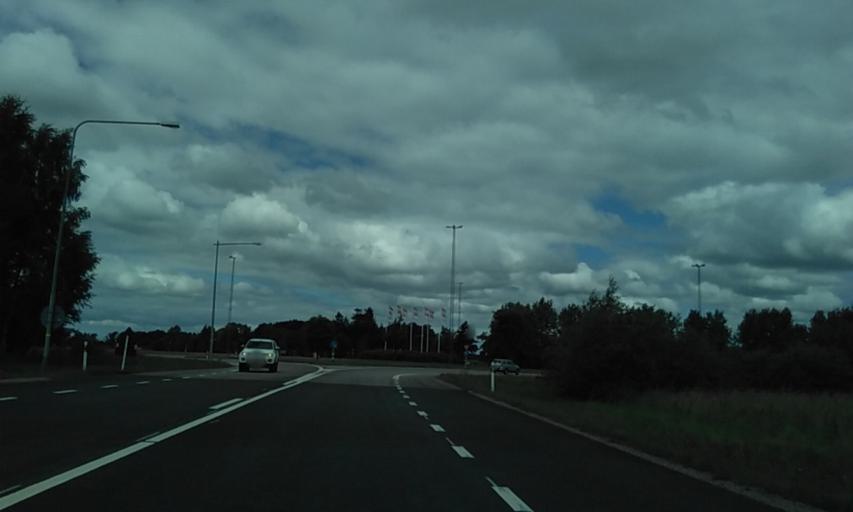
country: SE
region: Vaestra Goetaland
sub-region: Skara Kommun
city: Skara
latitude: 58.3806
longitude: 13.4101
